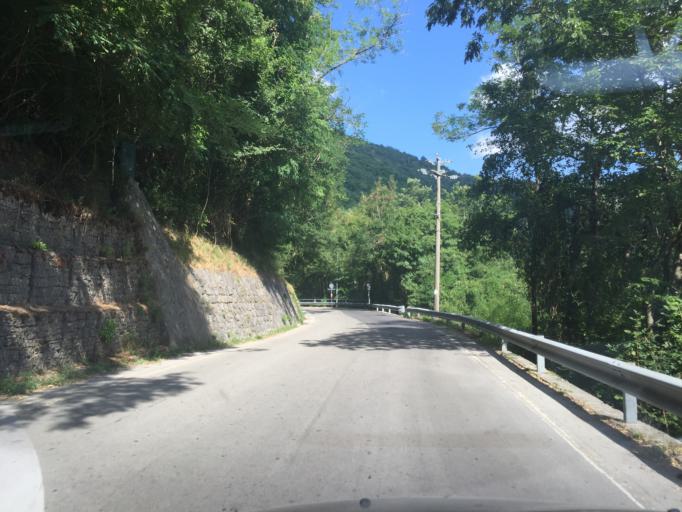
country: IT
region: Tuscany
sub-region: Provincia di Lucca
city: Careggine
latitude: 44.1266
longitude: 10.3032
